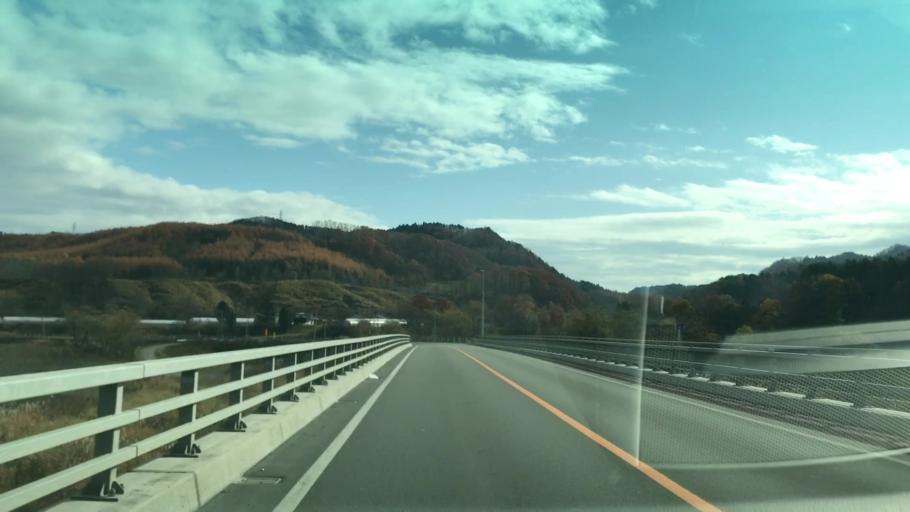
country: JP
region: Hokkaido
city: Shizunai-furukawacho
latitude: 42.7260
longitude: 142.3126
